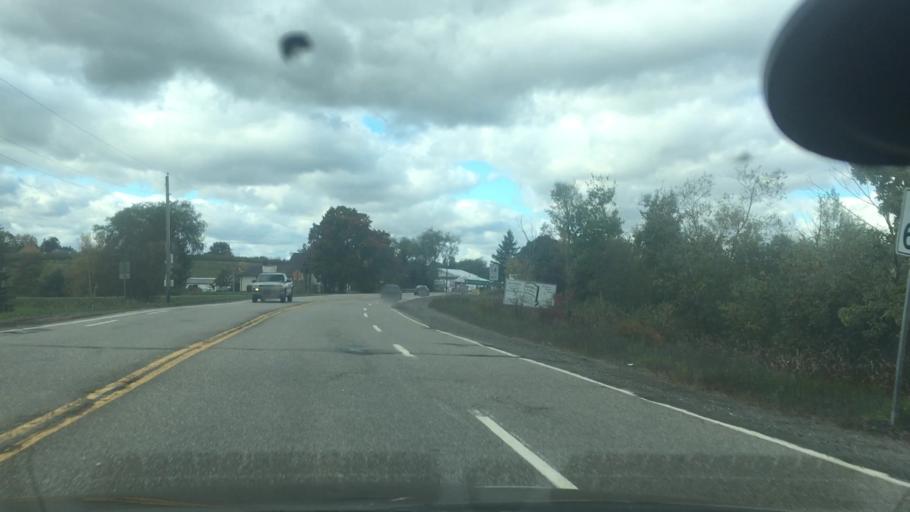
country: CA
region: Nova Scotia
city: Windsor
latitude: 44.9735
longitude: -64.1005
